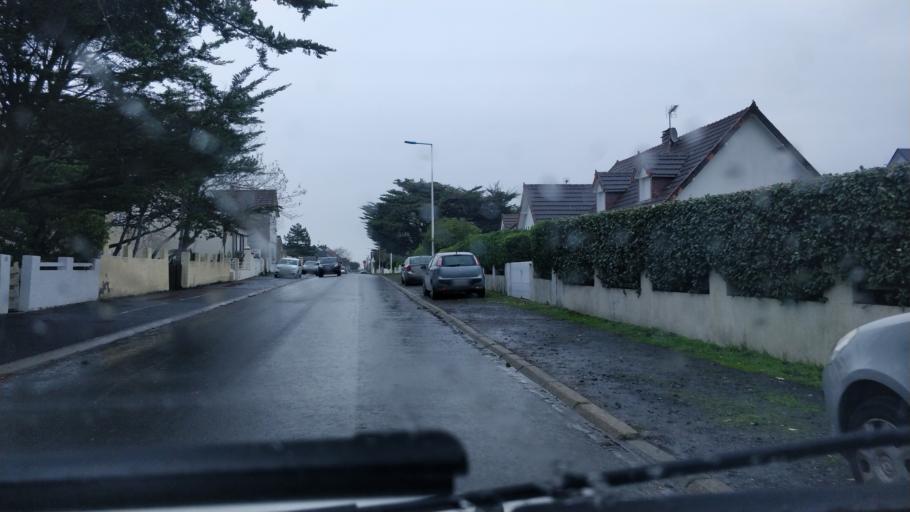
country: FR
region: Lower Normandy
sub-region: Departement de la Manche
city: Donville-les-Bains
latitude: 48.8941
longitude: -1.5696
